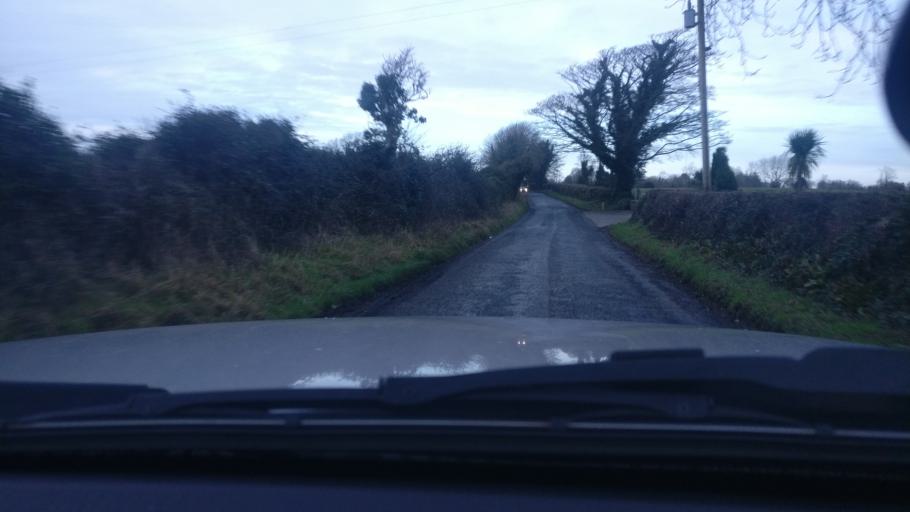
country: IE
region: Connaught
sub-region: County Galway
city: Loughrea
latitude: 53.1746
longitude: -8.5086
